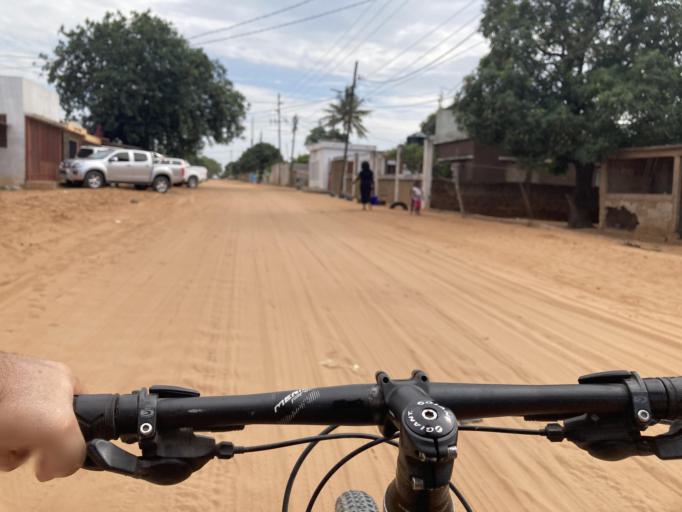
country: MZ
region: Maputo City
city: Maputo
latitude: -25.8958
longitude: 32.6071
